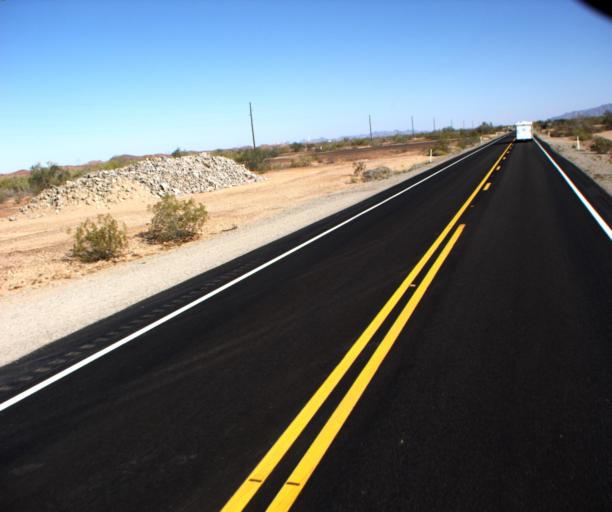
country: US
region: Arizona
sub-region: Yuma County
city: Wellton
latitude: 32.9794
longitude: -114.2893
